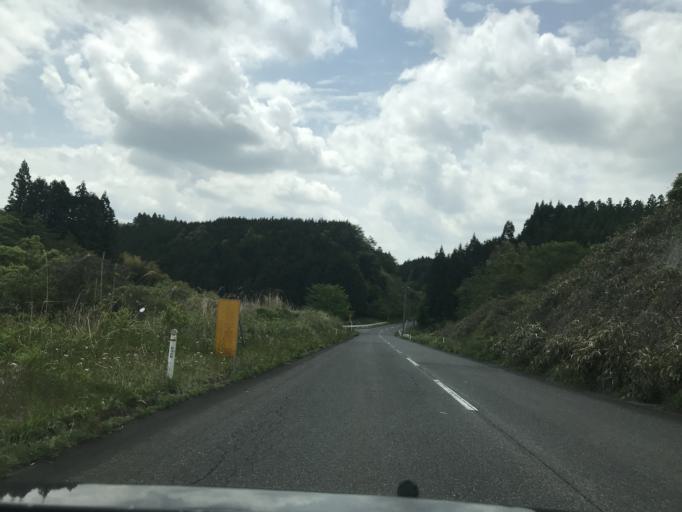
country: JP
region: Miyagi
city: Furukawa
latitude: 38.7159
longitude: 140.9204
